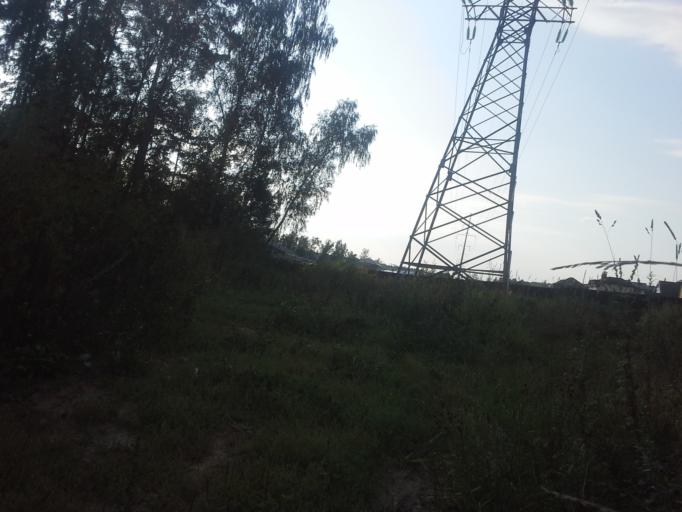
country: RU
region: Moskovskaya
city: Filimonki
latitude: 55.5412
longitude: 37.3377
